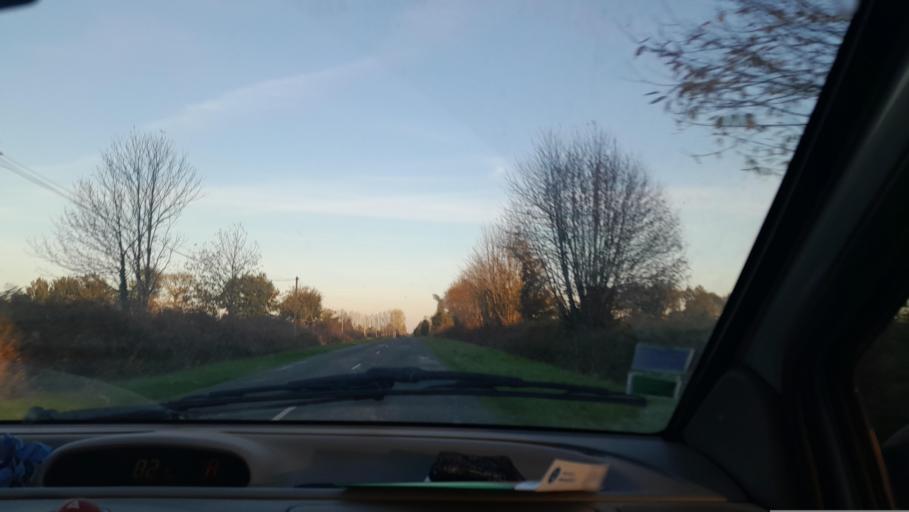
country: FR
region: Brittany
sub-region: Departement d'Ille-et-Vilaine
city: Le Pertre
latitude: 47.9674
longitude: -1.0711
